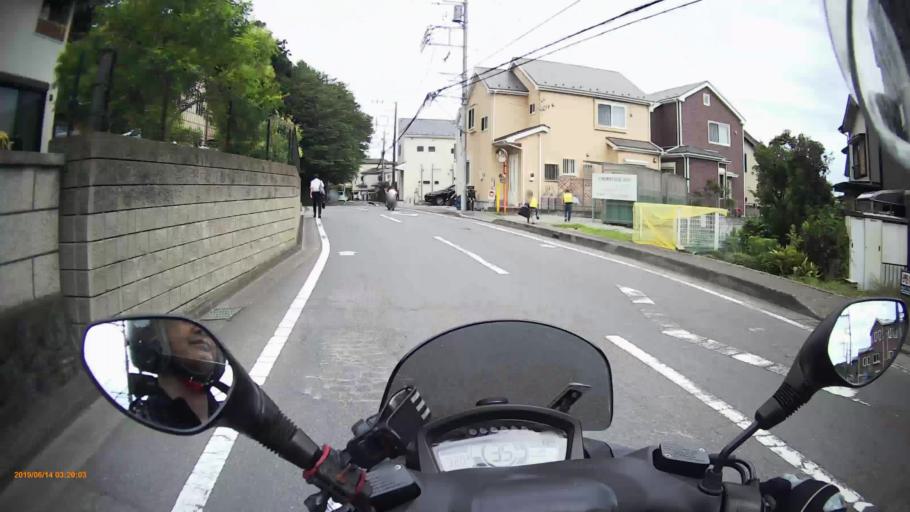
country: JP
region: Kanagawa
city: Minami-rinkan
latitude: 35.4126
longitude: 139.4534
